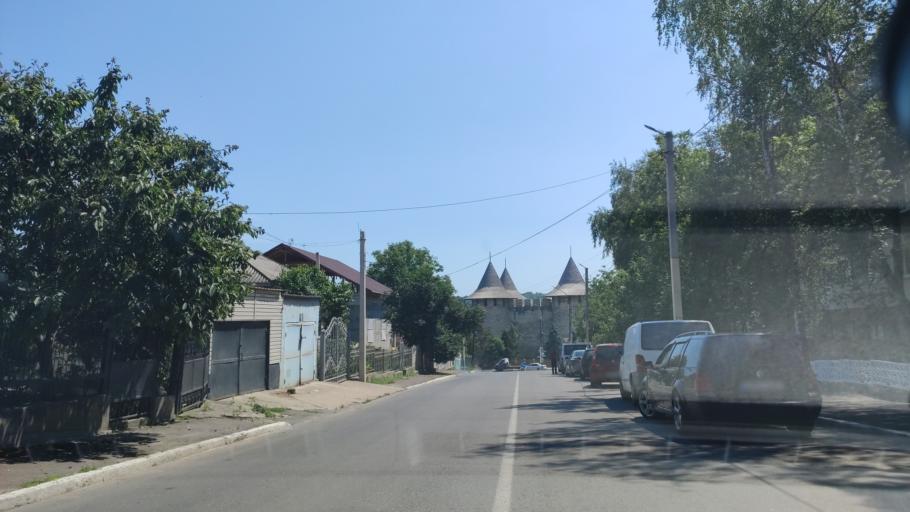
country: MD
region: Raionul Soroca
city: Soroca
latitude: 48.1617
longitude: 28.3025
